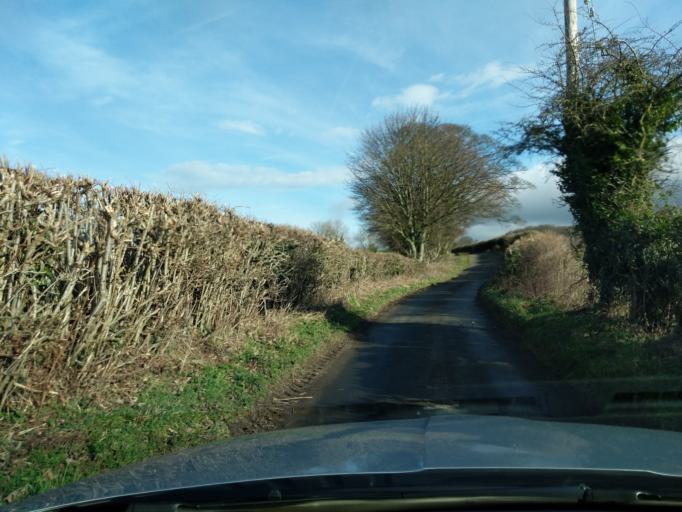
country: GB
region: England
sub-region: North Yorkshire
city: Catterick Garrison
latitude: 54.3373
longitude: -1.6954
